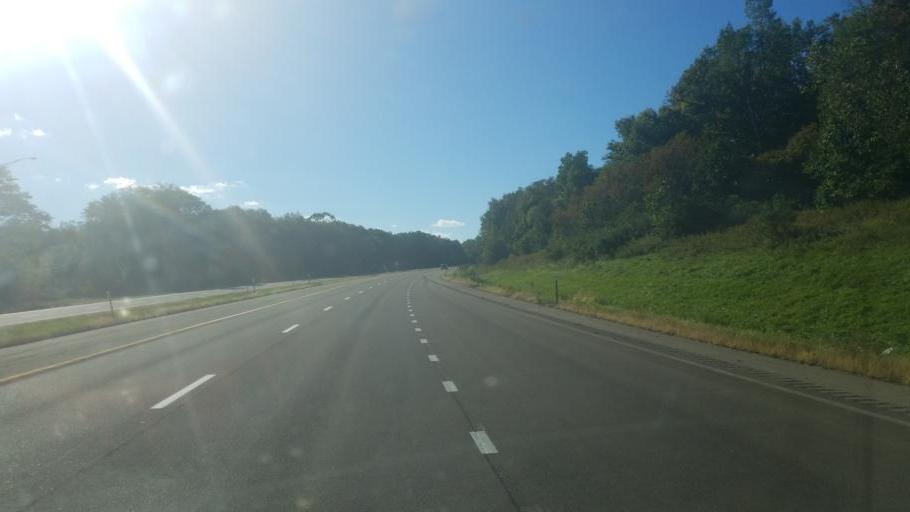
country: US
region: New York
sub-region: Cattaraugus County
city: Saint Bonaventure
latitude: 42.0885
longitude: -78.4591
